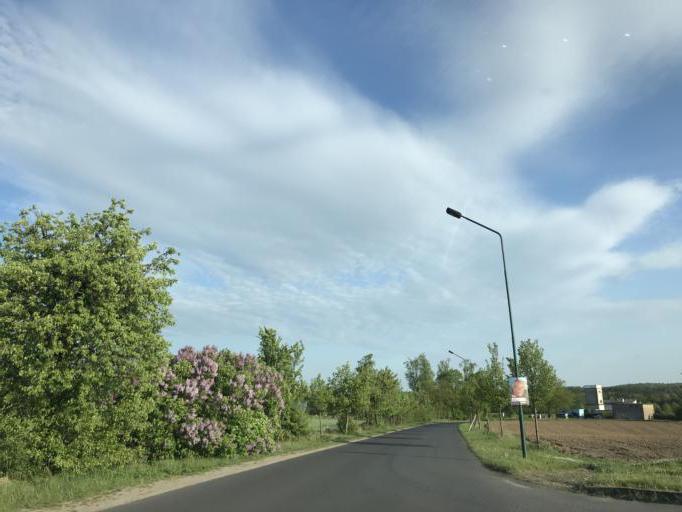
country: DE
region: Brandenburg
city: Joachimsthal
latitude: 52.9699
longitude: 13.7492
